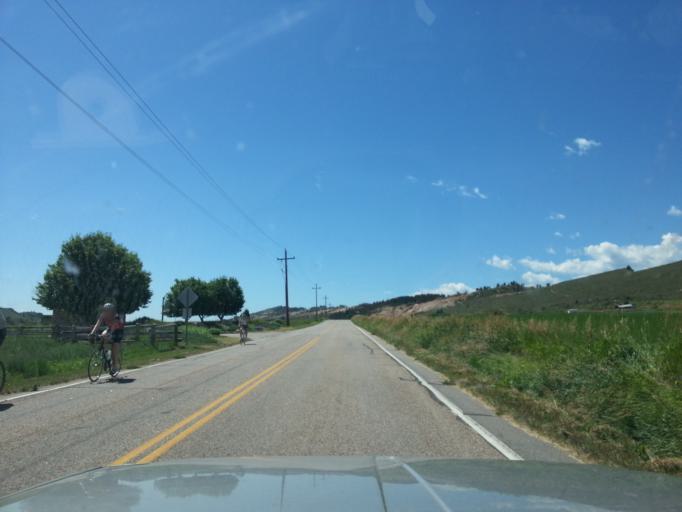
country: US
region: Colorado
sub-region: Larimer County
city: Loveland
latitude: 40.4666
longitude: -105.2067
